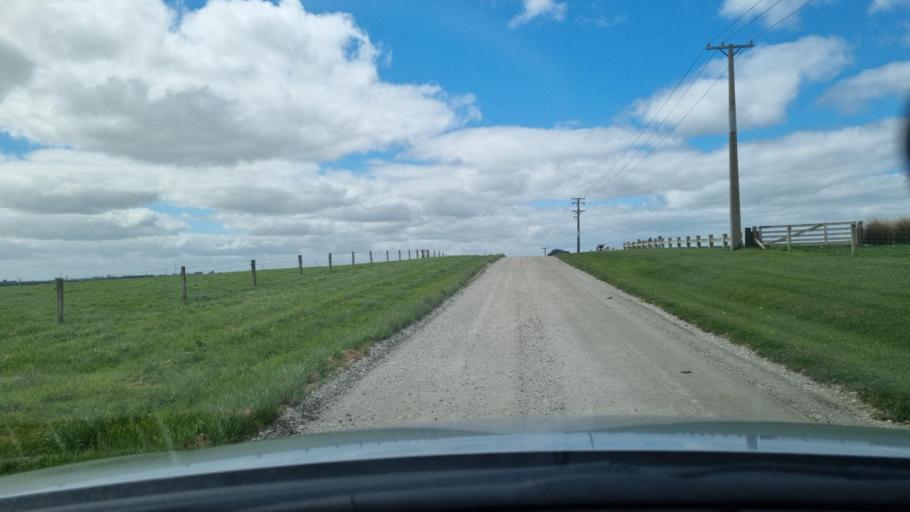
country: NZ
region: Southland
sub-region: Invercargill City
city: Invercargill
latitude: -46.4506
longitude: 168.4168
